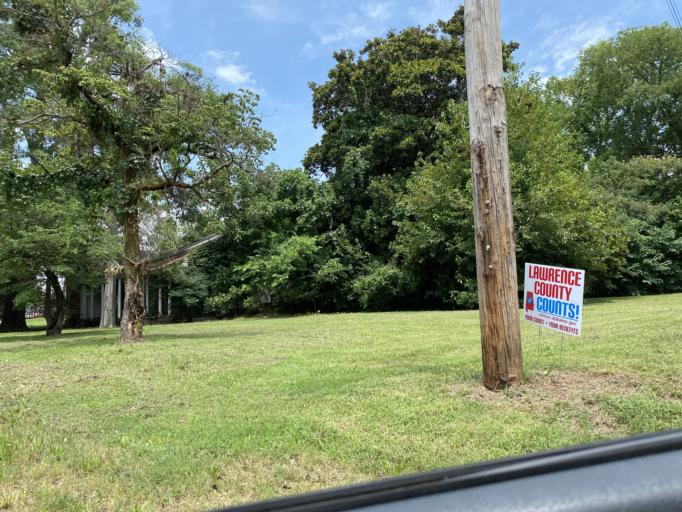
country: US
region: Alabama
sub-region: Lawrence County
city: Town Creek
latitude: 34.6691
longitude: -87.3091
